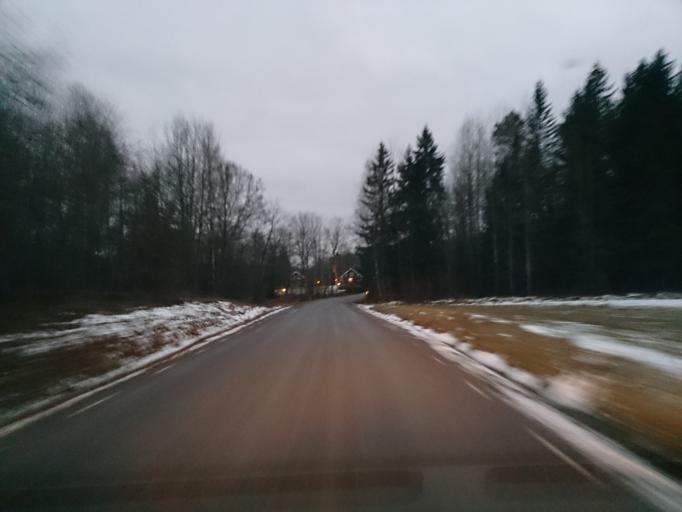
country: SE
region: OEstergoetland
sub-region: Atvidabergs Kommun
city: Atvidaberg
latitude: 58.2480
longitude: 16.1005
